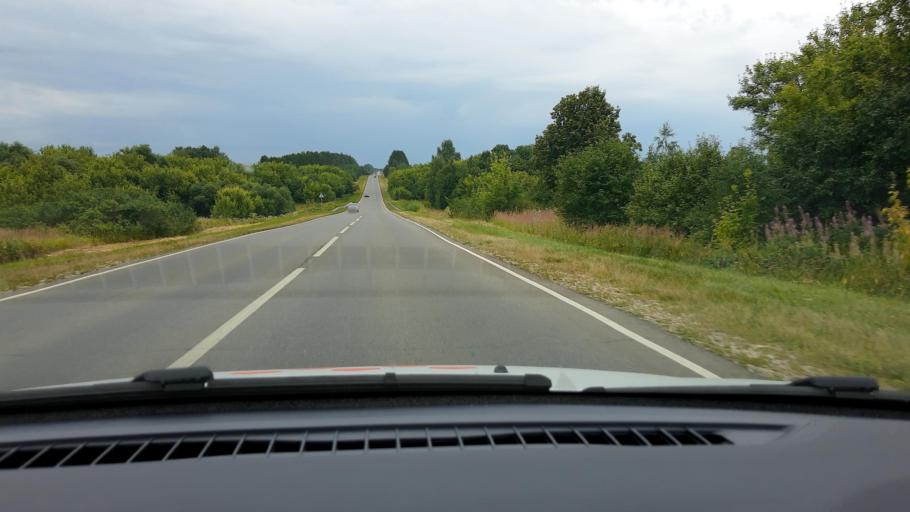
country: RU
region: Nizjnij Novgorod
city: Sarov
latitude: 55.1448
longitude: 43.5626
